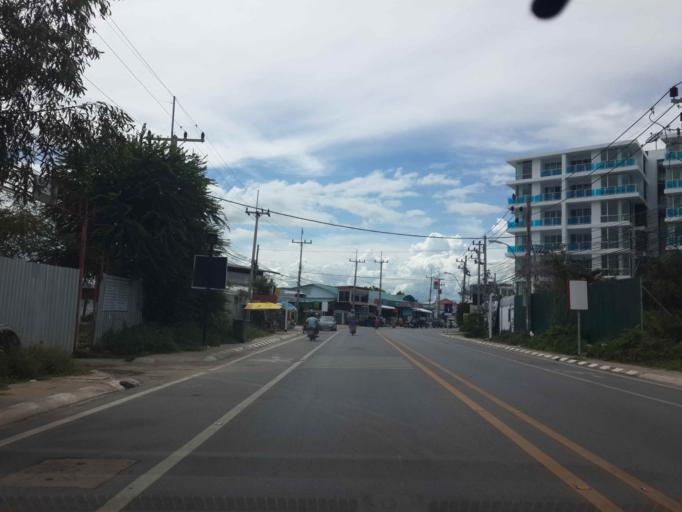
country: TH
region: Prachuap Khiri Khan
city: Hua Hin
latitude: 12.5292
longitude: 99.9682
